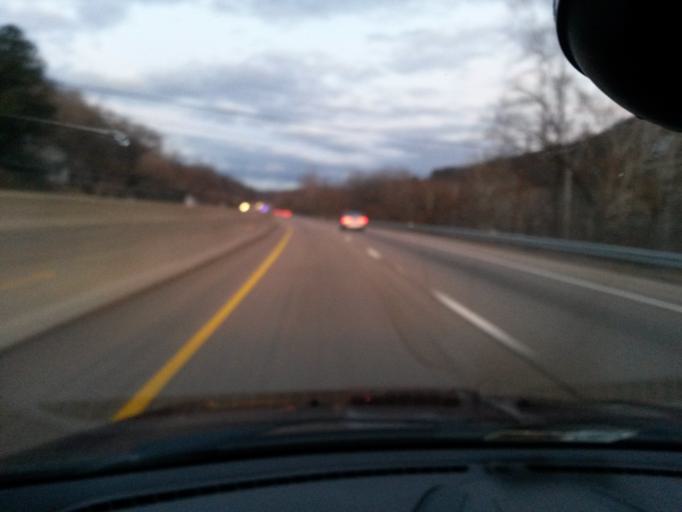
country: US
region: Virginia
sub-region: City of Covington
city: Fairlawn
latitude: 37.7719
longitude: -79.9490
